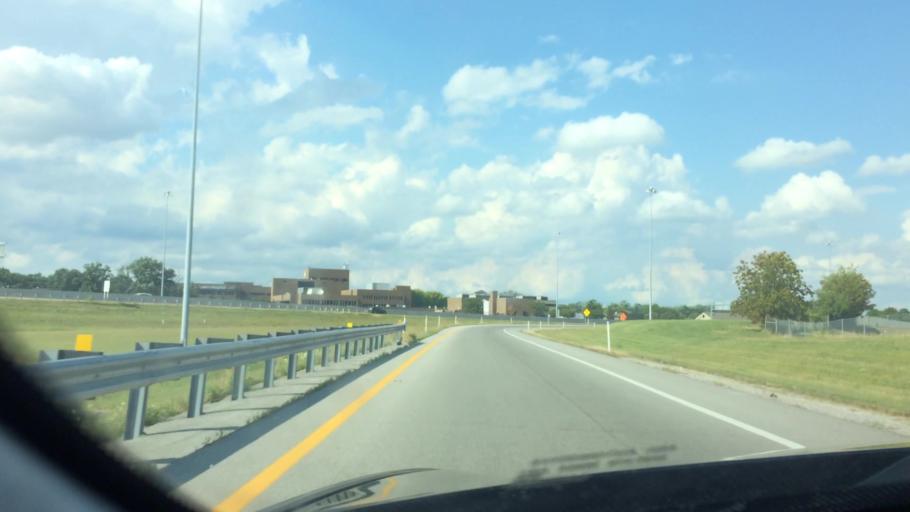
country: US
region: Ohio
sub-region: Lucas County
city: Maumee
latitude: 41.5534
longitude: -83.6831
